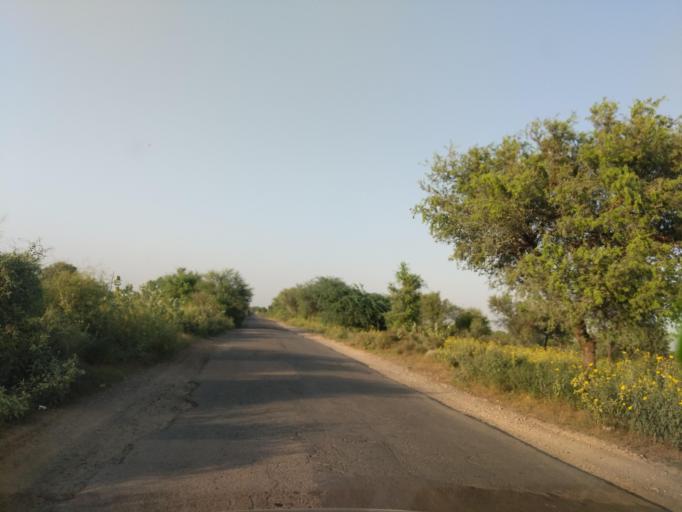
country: IN
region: Rajasthan
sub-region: Churu
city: Rajgarh
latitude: 28.5762
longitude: 75.3708
